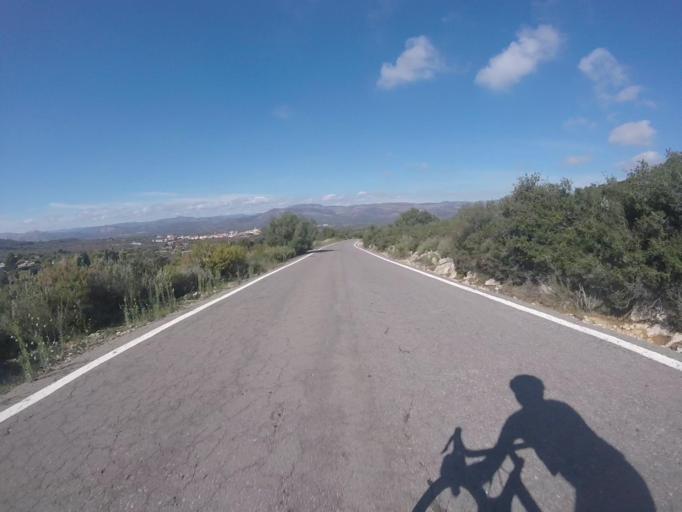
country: ES
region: Valencia
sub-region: Provincia de Castello
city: Albocasser
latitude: 40.3537
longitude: 0.0428
